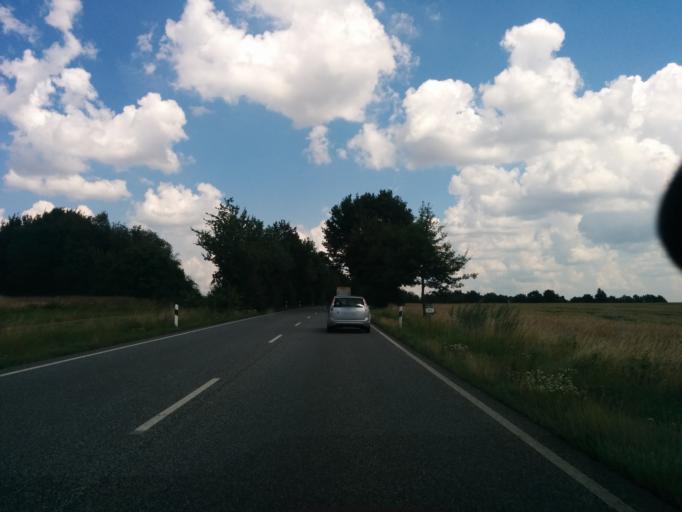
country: DE
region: Lower Saxony
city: Wollbrandshausen
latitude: 51.5884
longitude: 10.1514
